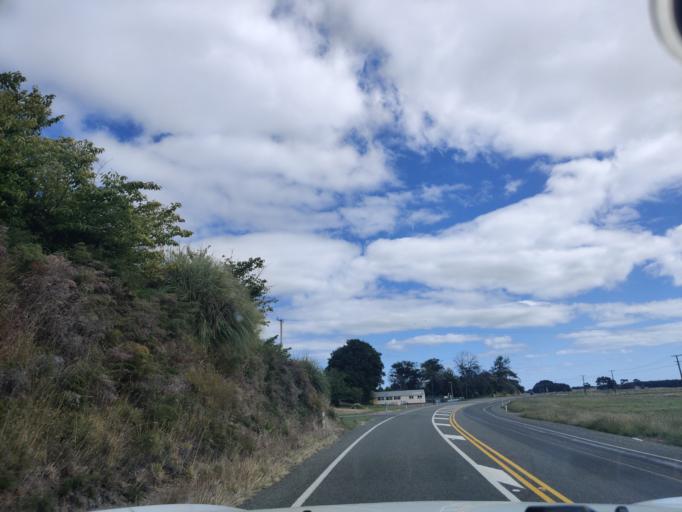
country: NZ
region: Manawatu-Wanganui
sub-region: Horowhenua District
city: Foxton
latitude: -40.4095
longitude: 175.3796
